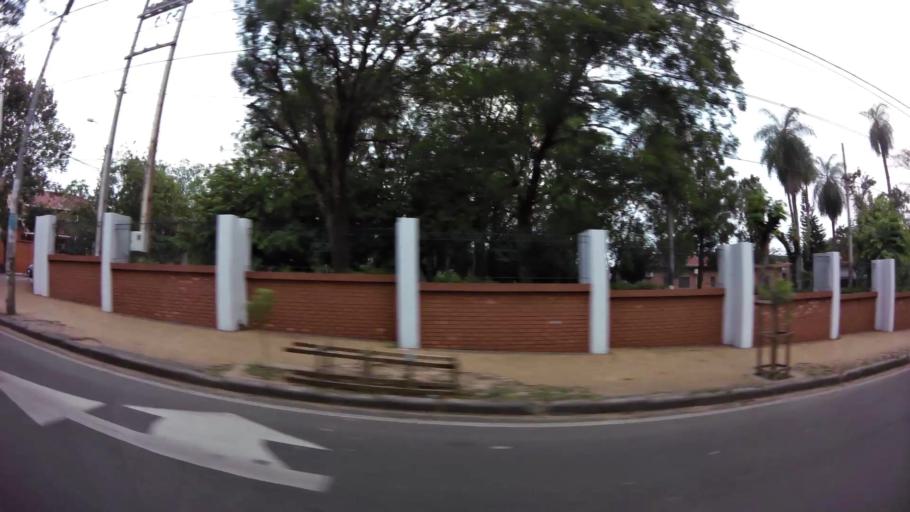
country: PY
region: Asuncion
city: Asuncion
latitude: -25.3225
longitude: -57.6232
